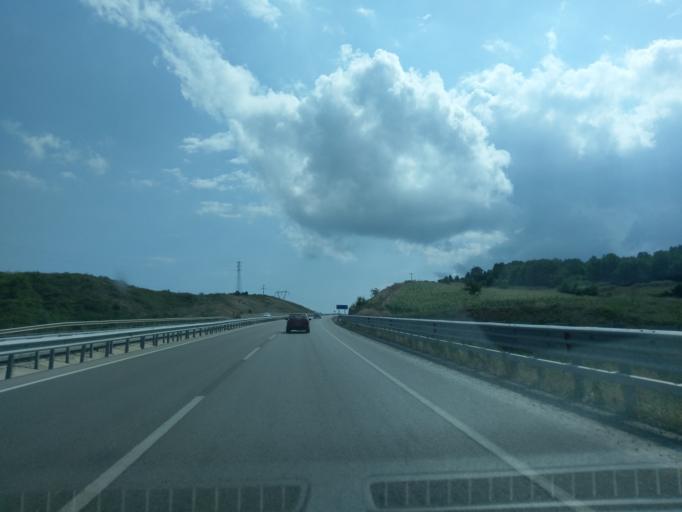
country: TR
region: Sinop
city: Kabali
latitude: 41.8554
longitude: 35.1136
